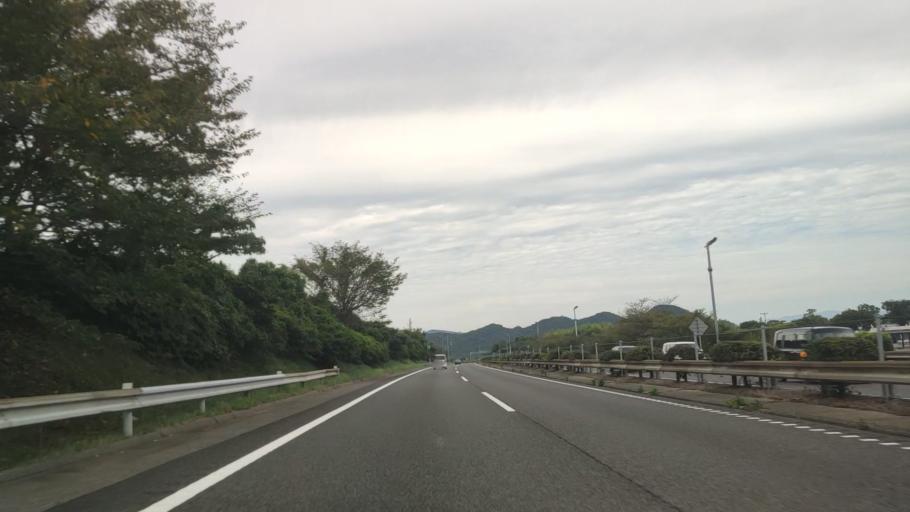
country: JP
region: Shiga Prefecture
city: Youkaichi
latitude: 35.0784
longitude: 136.1941
